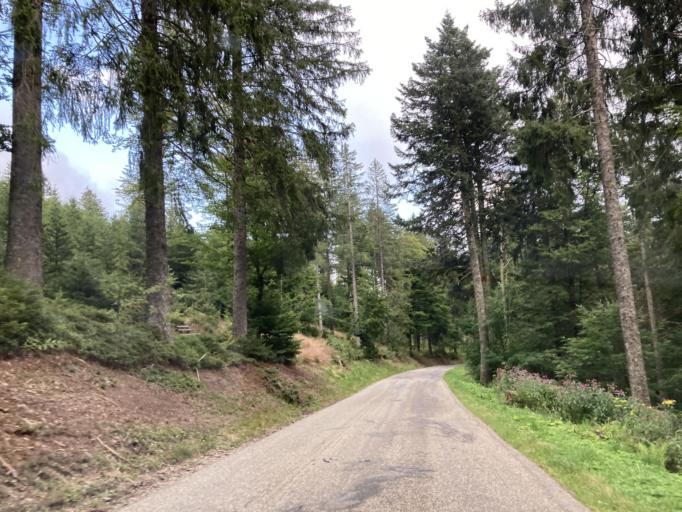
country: DE
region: Baden-Wuerttemberg
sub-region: Freiburg Region
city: Furtwangen im Schwarzwald
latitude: 48.0599
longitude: 8.1885
